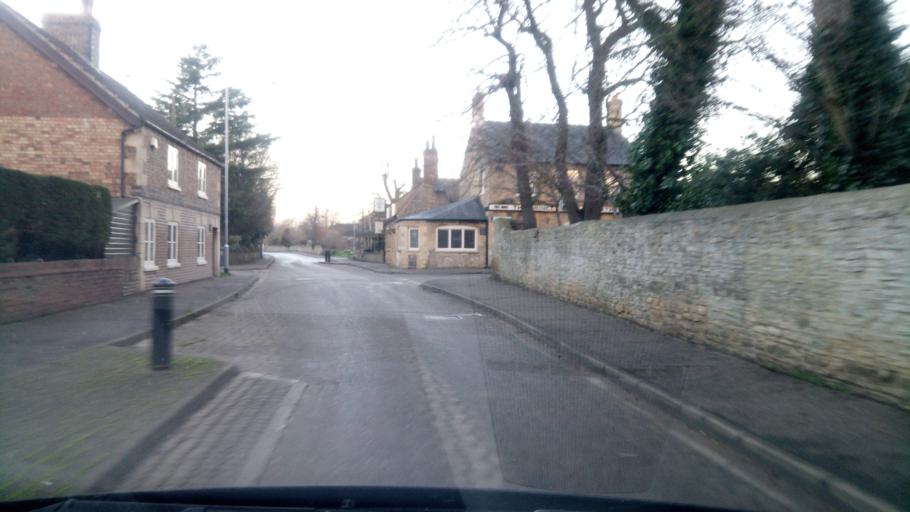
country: GB
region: England
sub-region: Peterborough
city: Castor
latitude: 52.5729
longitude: -0.3462
